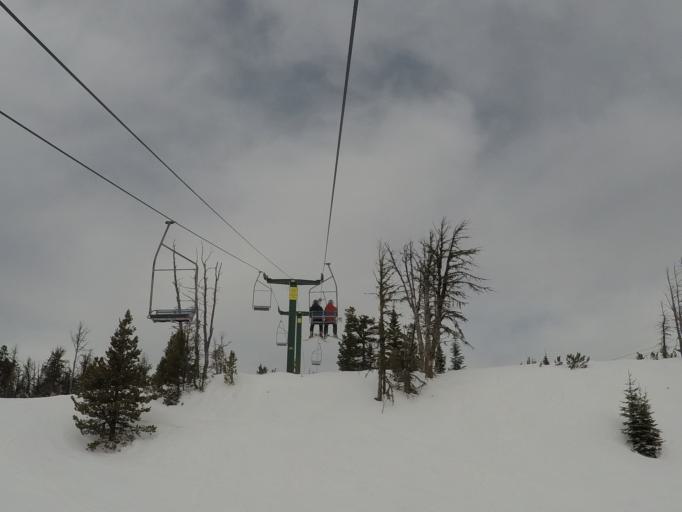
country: US
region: Montana
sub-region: Meagher County
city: White Sulphur Springs
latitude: 46.8374
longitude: -110.7156
